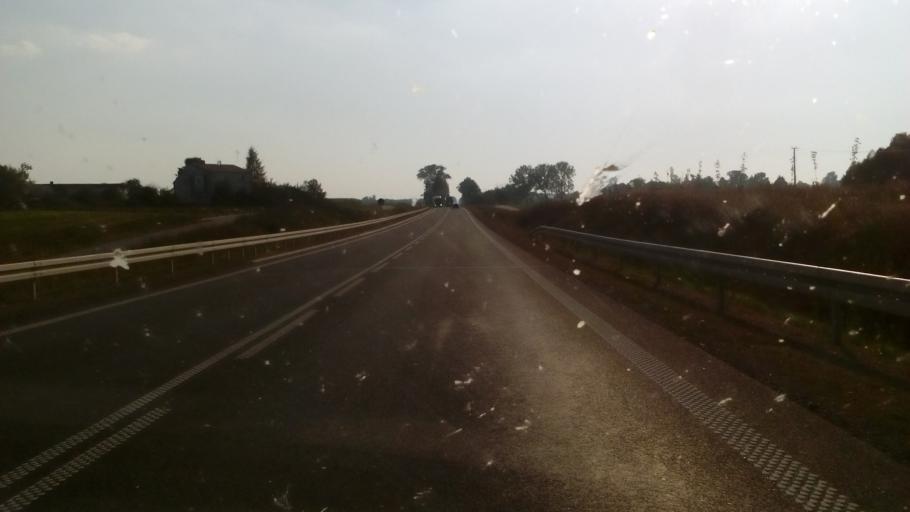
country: PL
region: Podlasie
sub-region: Powiat augustowski
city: Augustow
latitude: 53.7841
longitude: 22.8482
